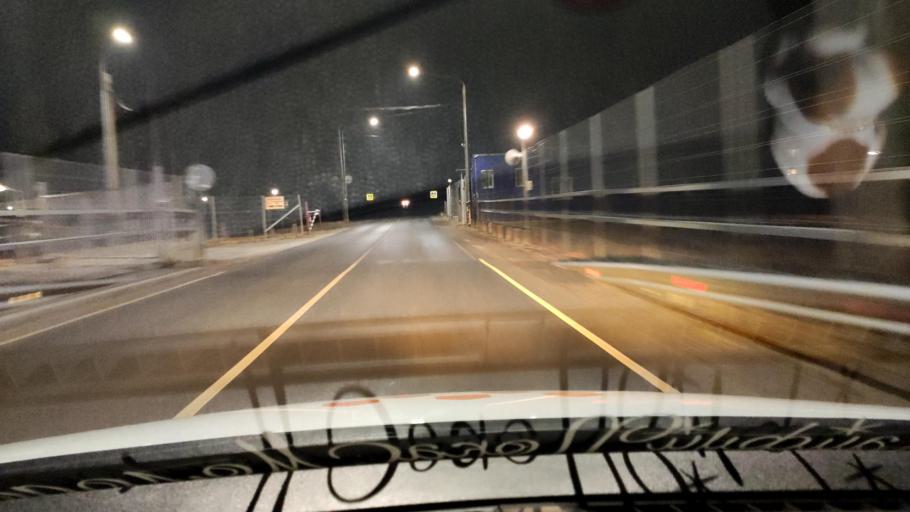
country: RU
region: Voronezj
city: Shilovo
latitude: 51.5375
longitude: 39.1388
